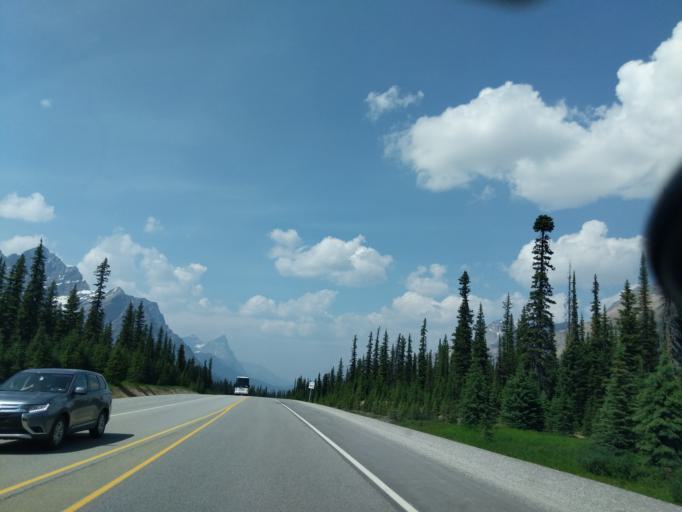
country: CA
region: Alberta
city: Lake Louise
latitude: 51.7206
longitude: -116.4950
